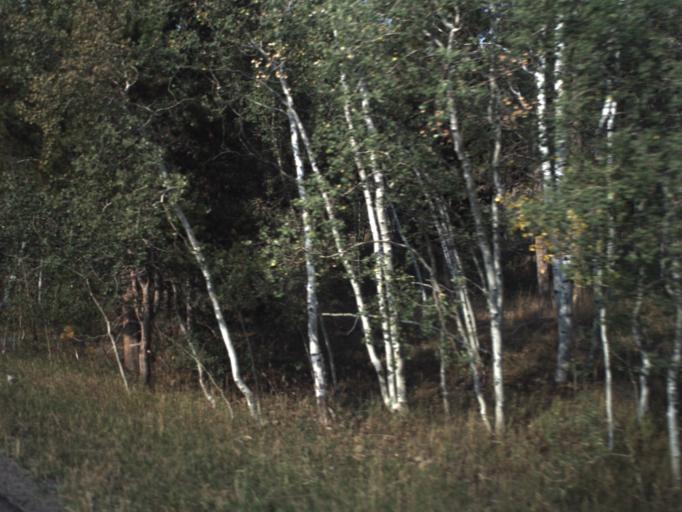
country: US
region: Wyoming
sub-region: Uinta County
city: Evanston
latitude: 40.9267
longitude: -110.8285
